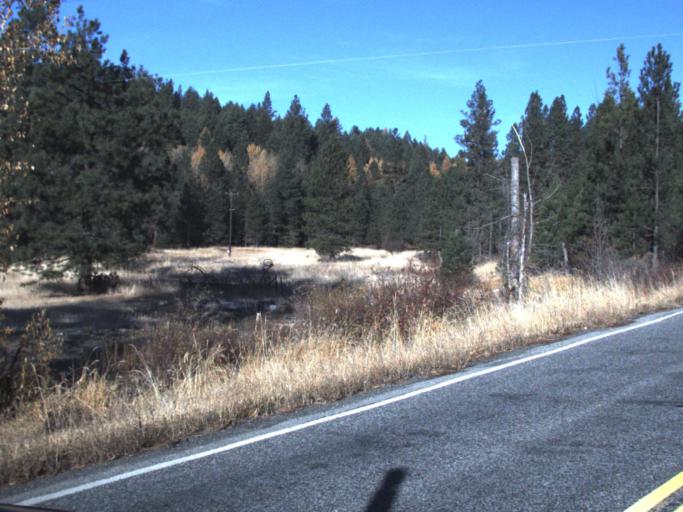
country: US
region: Washington
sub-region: Ferry County
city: Republic
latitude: 48.6349
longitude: -118.7302
